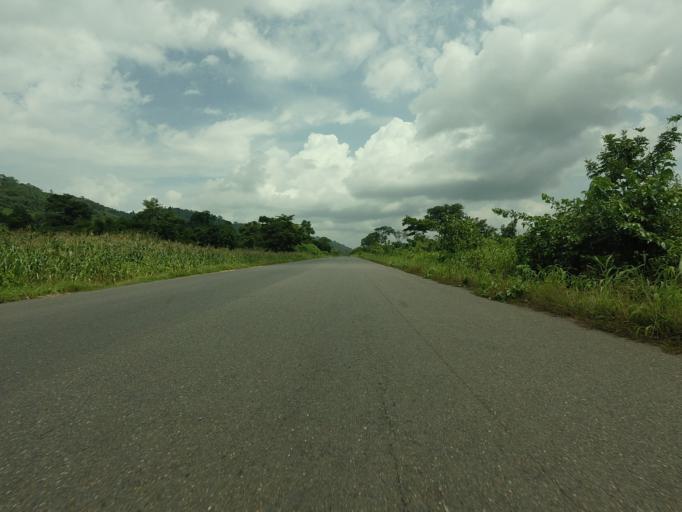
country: GH
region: Volta
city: Ho
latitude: 6.4923
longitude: 0.2013
